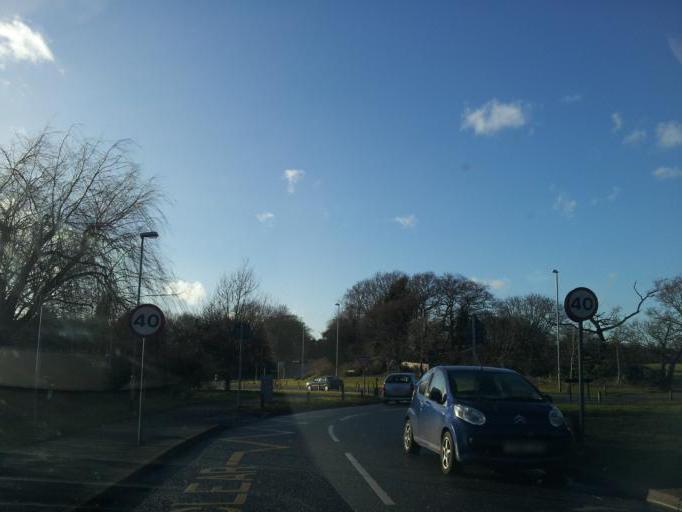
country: GB
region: England
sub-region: Nottinghamshire
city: South Collingham
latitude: 53.0808
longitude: -0.7593
